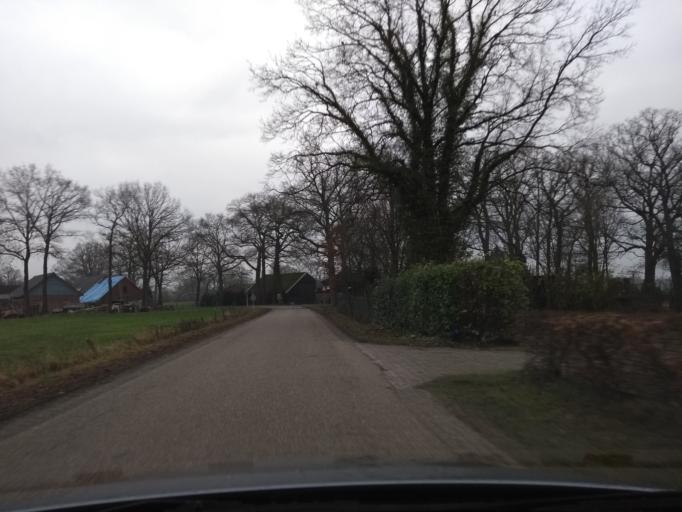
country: NL
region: Overijssel
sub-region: Gemeente Almelo
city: Almelo
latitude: 52.3223
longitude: 6.6923
